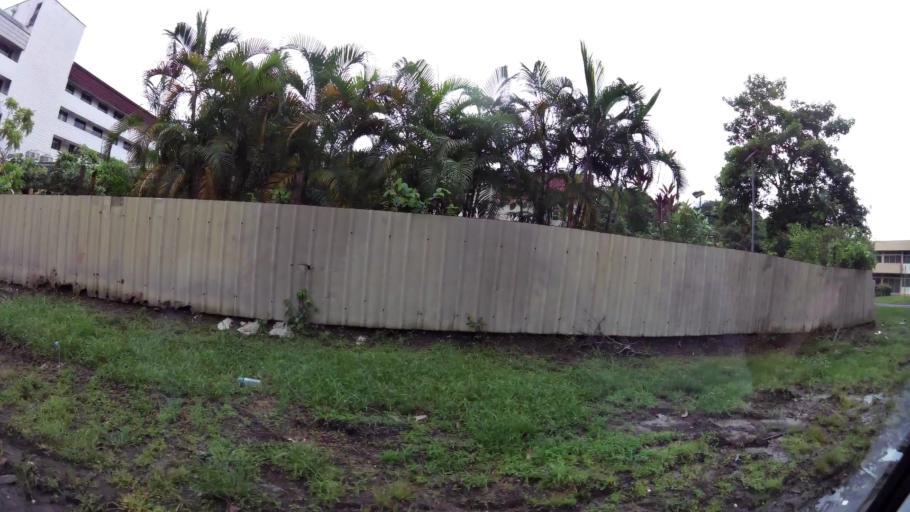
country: BN
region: Brunei and Muara
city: Bandar Seri Begawan
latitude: 4.8952
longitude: 114.9421
